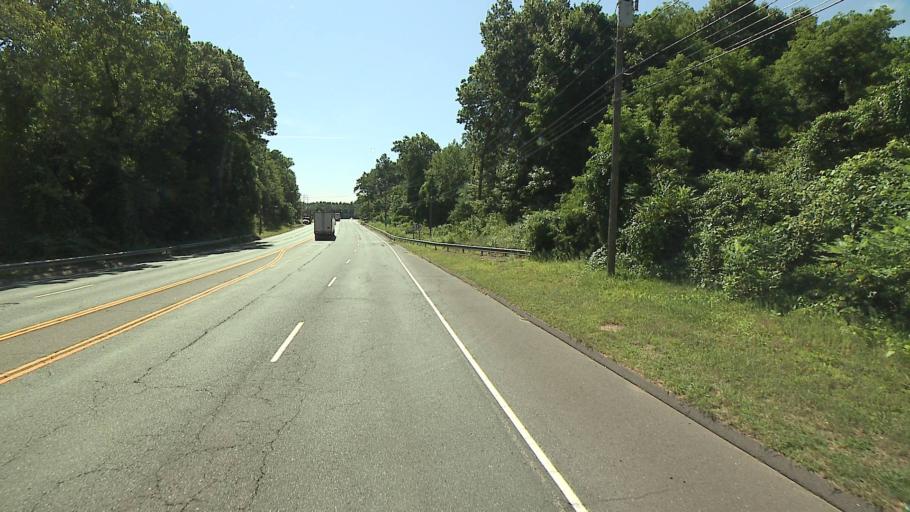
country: US
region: Connecticut
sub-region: Hartford County
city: Blue Hills
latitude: 41.8572
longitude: -72.7082
